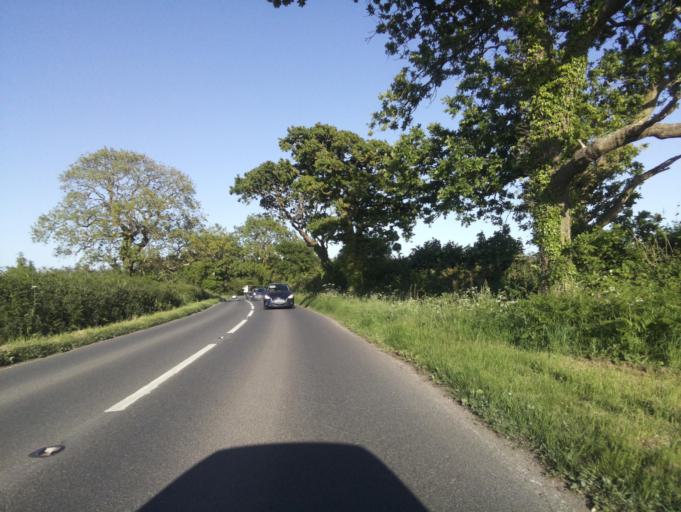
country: GB
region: England
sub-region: Devon
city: Colyton
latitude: 50.7127
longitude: -3.1346
